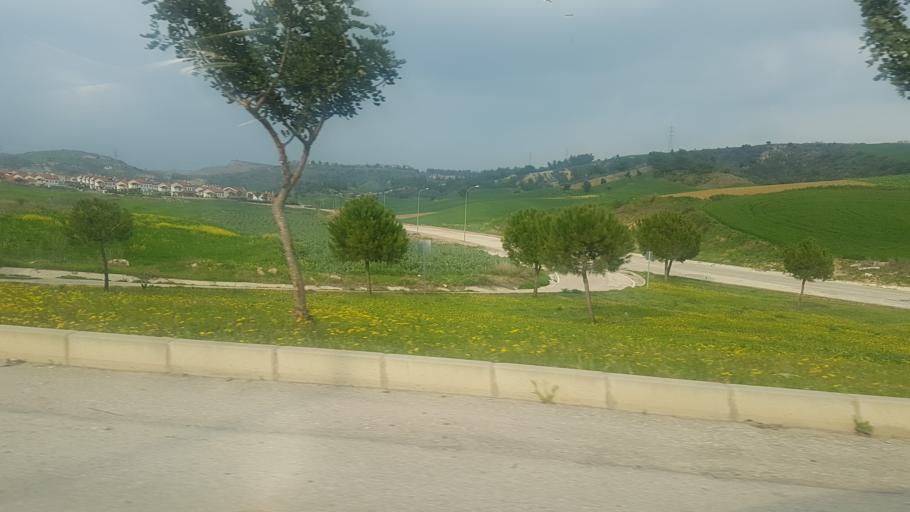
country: TR
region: Adana
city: Seyhan
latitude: 37.0478
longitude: 35.1784
